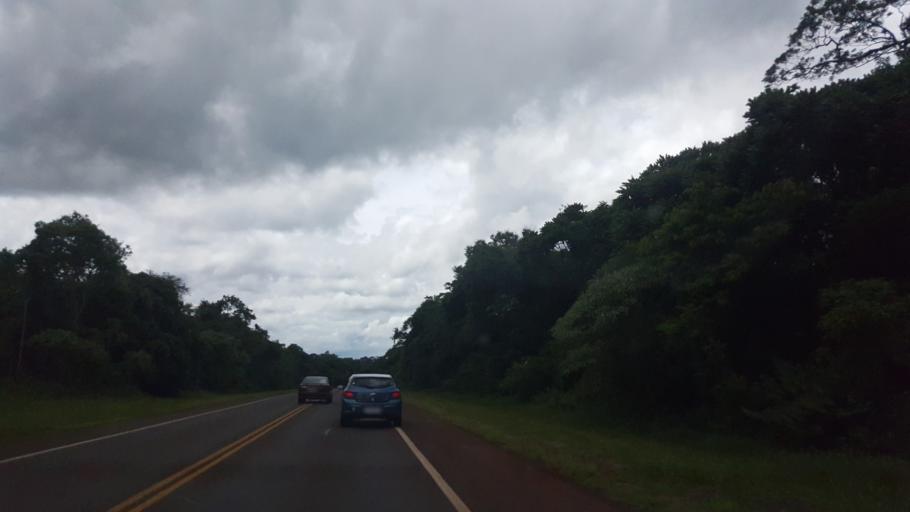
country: AR
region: Misiones
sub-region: Departamento de Iguazu
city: Puerto Iguazu
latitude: -25.6959
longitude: -54.5148
